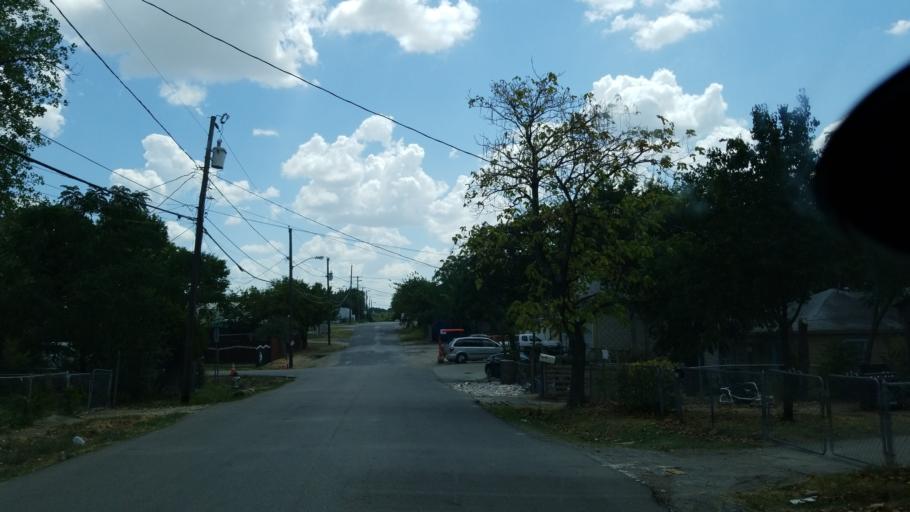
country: US
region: Texas
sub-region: Dallas County
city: Cockrell Hill
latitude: 32.7473
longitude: -96.9115
